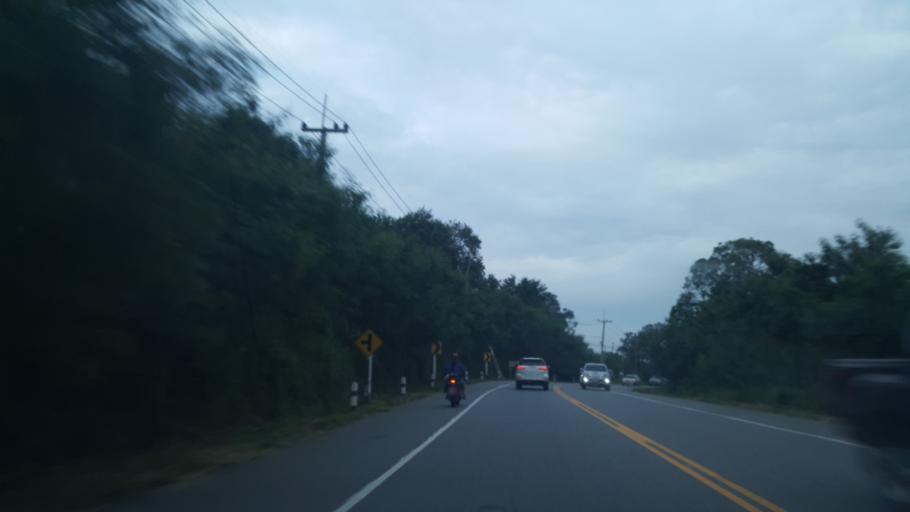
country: TH
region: Chon Buri
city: Ban Talat Bueng
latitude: 12.9579
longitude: 101.0173
